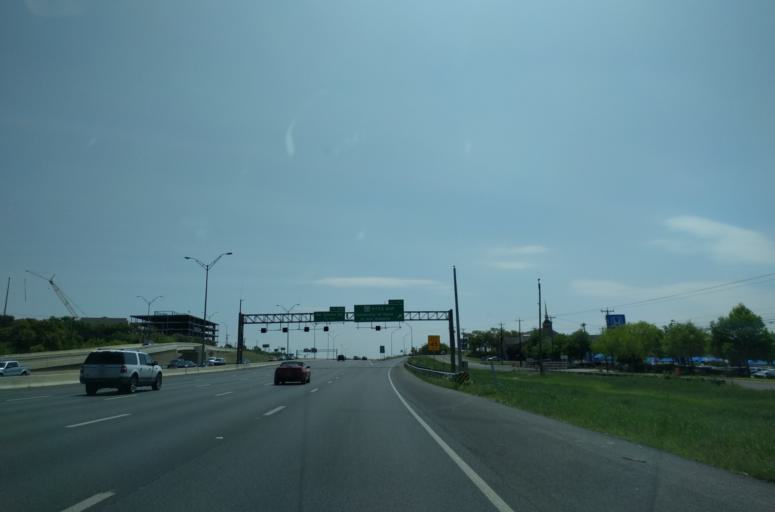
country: US
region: Texas
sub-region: Bexar County
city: Shavano Park
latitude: 29.5811
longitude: -98.5967
